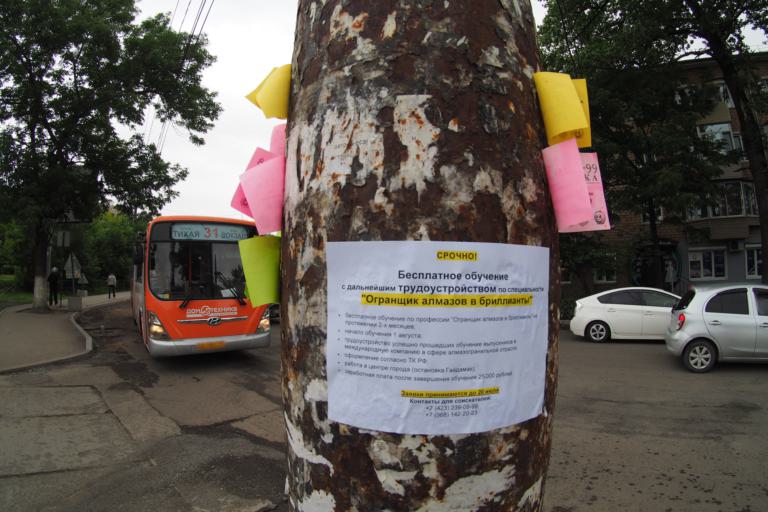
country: RU
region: Primorskiy
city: Vladivostok
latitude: 43.1047
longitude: 131.9381
